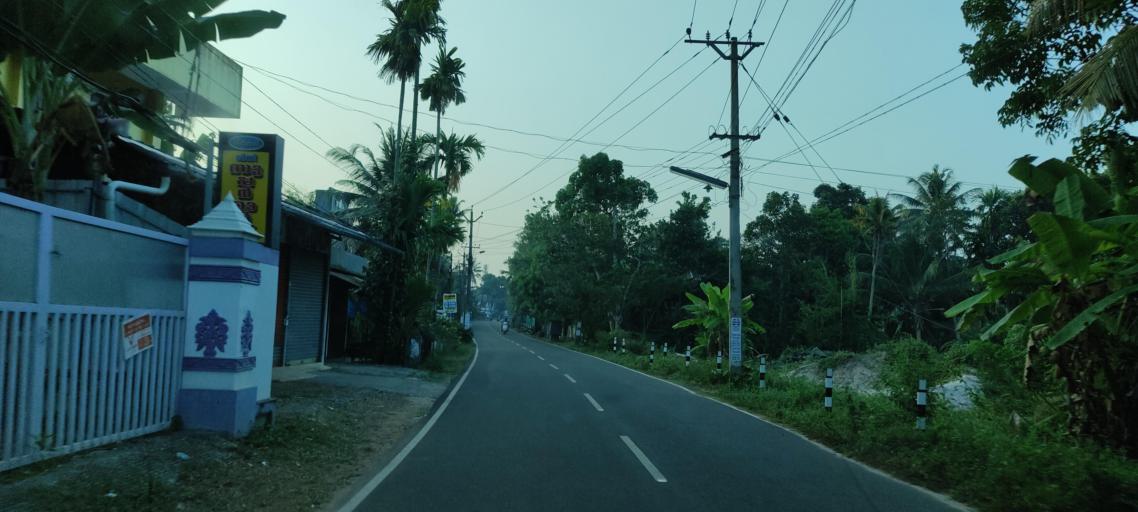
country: IN
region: Kerala
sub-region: Alappuzha
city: Alleppey
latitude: 9.4430
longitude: 76.3464
